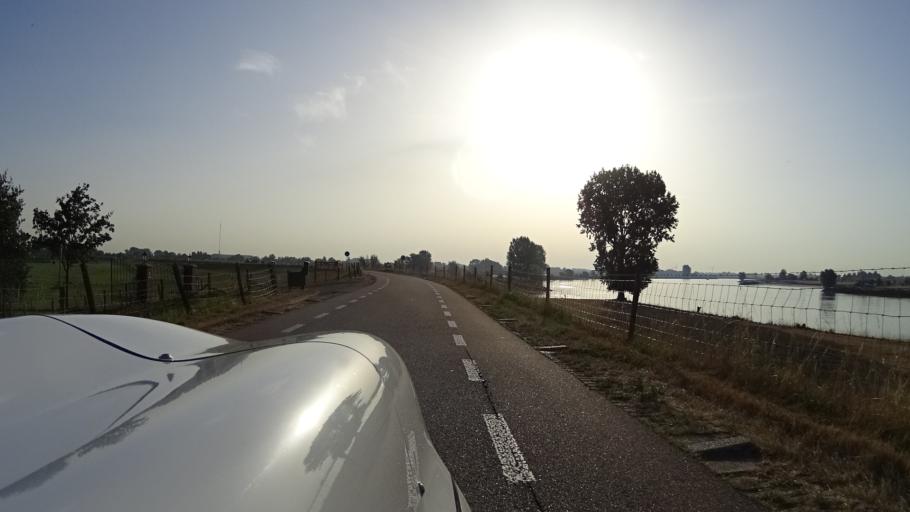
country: NL
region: Utrecht
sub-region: Gemeente Lopik
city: Lopik
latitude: 51.9778
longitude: 4.9936
